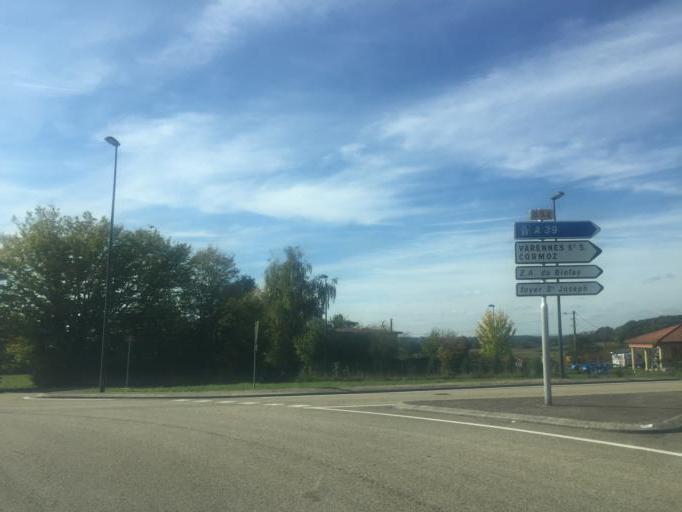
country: FR
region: Rhone-Alpes
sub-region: Departement de l'Ain
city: Marboz
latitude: 46.4121
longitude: 5.2687
